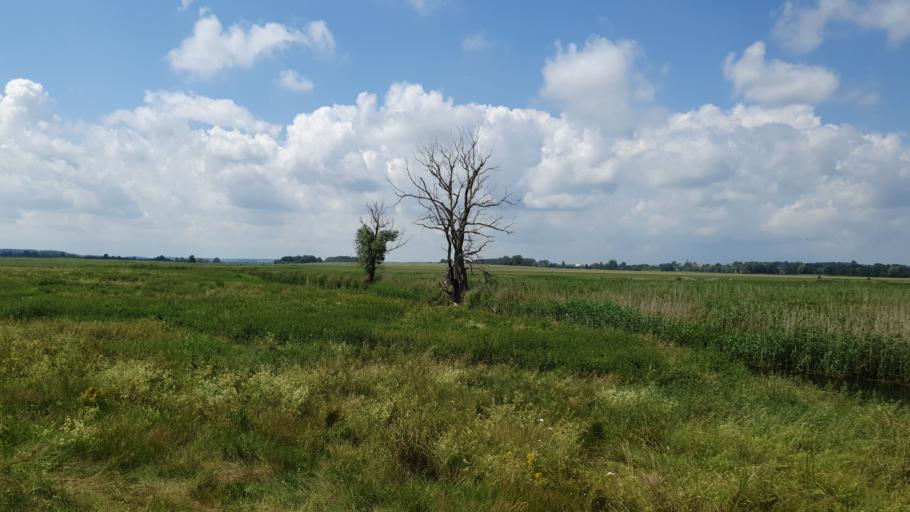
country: BY
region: Grodnenskaya
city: Mir
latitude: 53.3879
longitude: 26.3499
